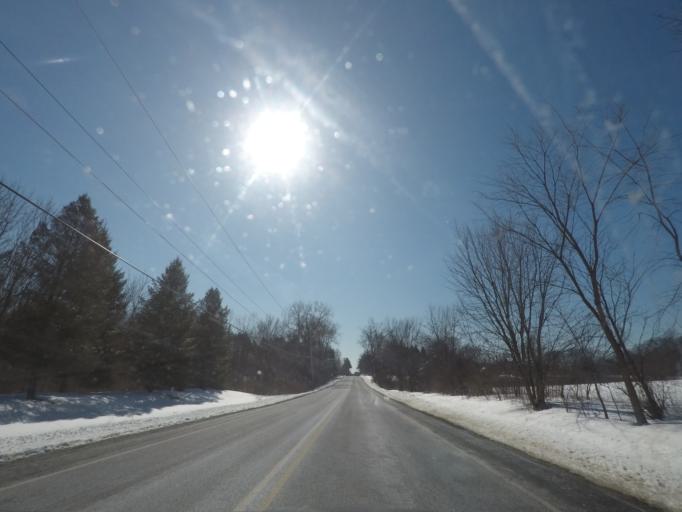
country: US
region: New York
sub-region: Saratoga County
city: Country Knolls
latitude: 42.9393
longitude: -73.8259
